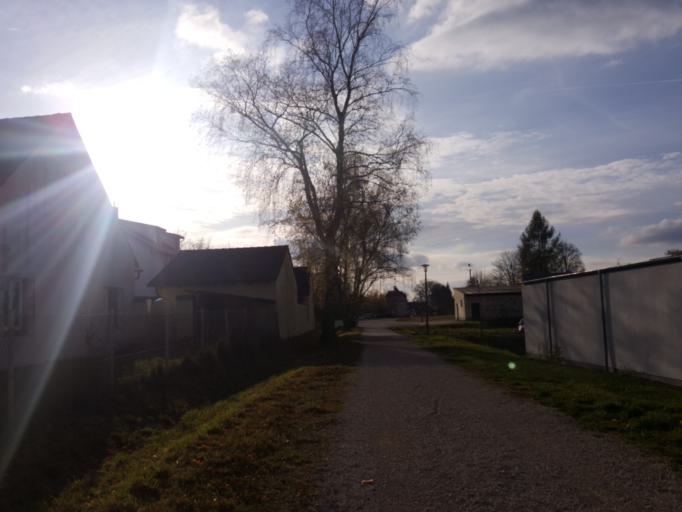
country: DE
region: Bavaria
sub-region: Regierungsbezirk Mittelfranken
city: Allersberg
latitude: 49.2532
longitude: 11.2464
